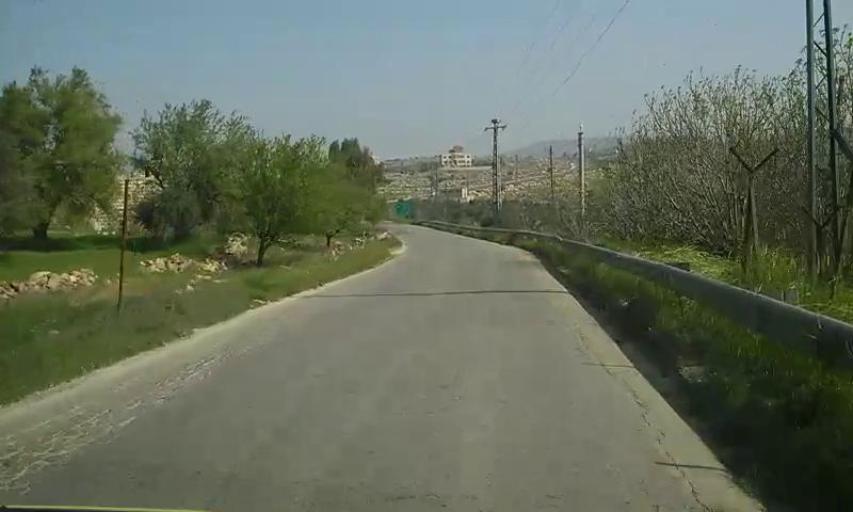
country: PS
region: West Bank
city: Silwad
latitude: 31.9617
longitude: 35.2626
